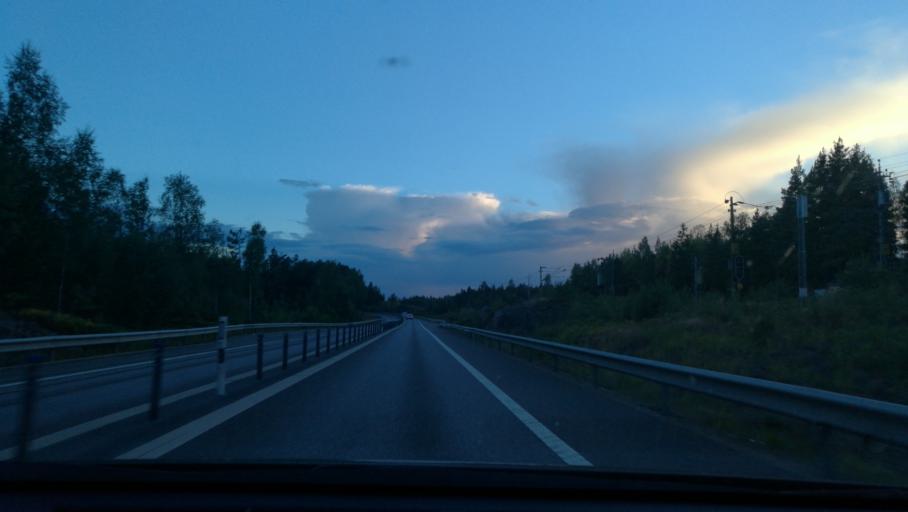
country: SE
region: OEstergoetland
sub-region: Norrkopings Kommun
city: Jursla
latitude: 58.8231
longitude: 16.1731
